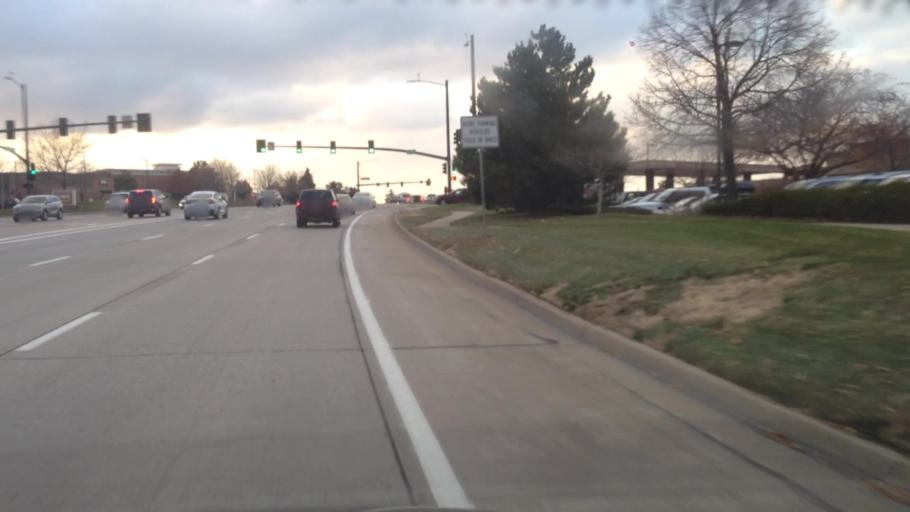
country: US
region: Colorado
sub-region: Douglas County
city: Highlands Ranch
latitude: 39.5436
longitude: -104.9422
